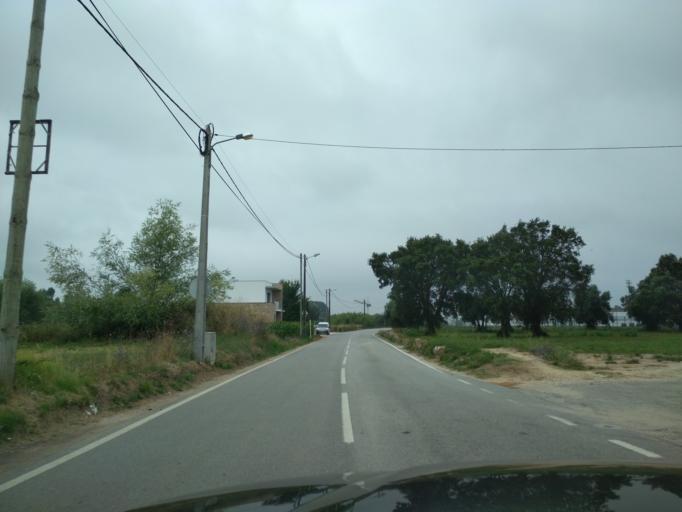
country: PT
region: Aveiro
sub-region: Mealhada
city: Mealhada
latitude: 40.3712
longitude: -8.4549
